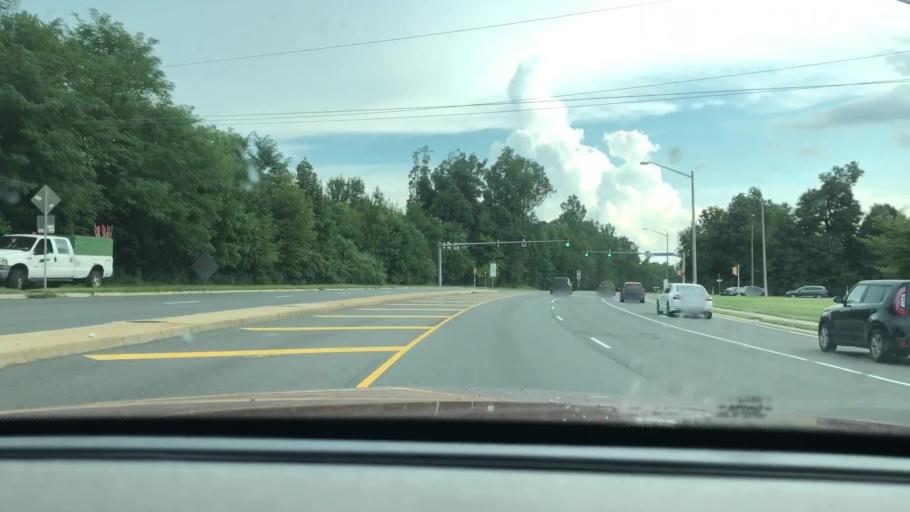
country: US
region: Virginia
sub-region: Fairfax County
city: Greenbriar
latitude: 38.8487
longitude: -77.4021
